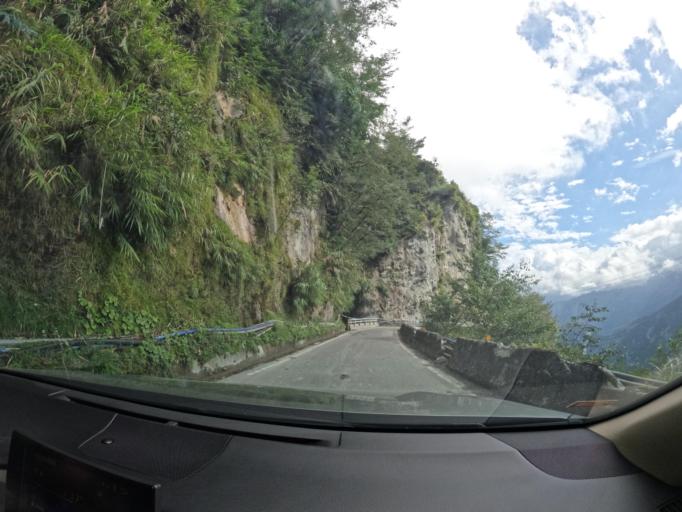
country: TW
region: Taiwan
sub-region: Taitung
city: Taitung
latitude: 23.2387
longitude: 121.0043
